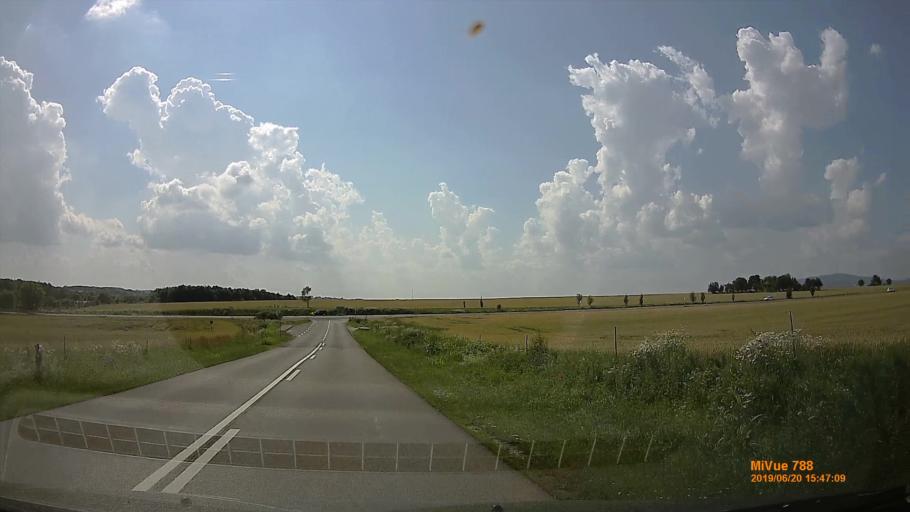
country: HU
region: Baranya
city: Kozarmisleny
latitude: 46.0029
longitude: 18.2368
